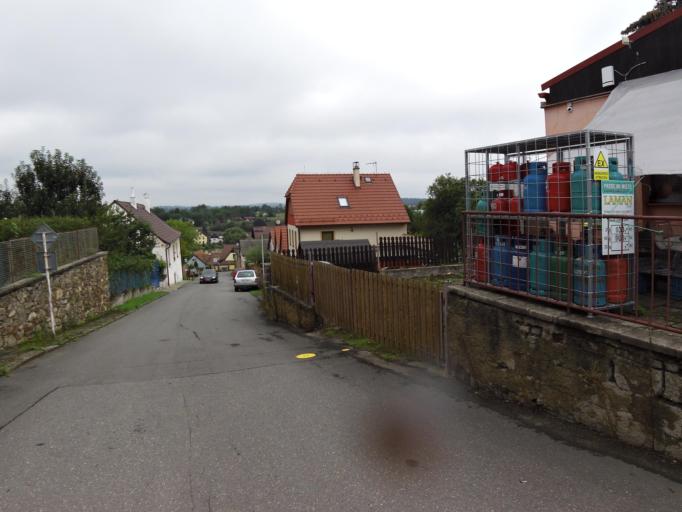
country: CZ
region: Jihocesky
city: Mlada Vozice
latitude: 49.5319
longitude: 14.8074
